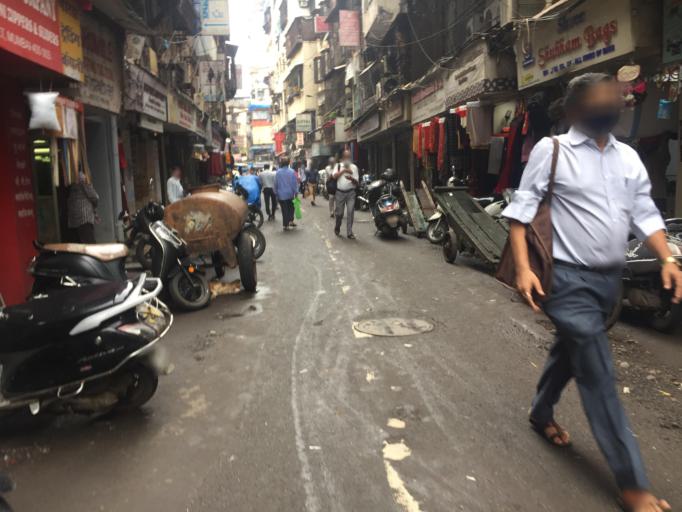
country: IN
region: Maharashtra
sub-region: Raigarh
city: Uran
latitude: 18.9506
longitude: 72.8321
